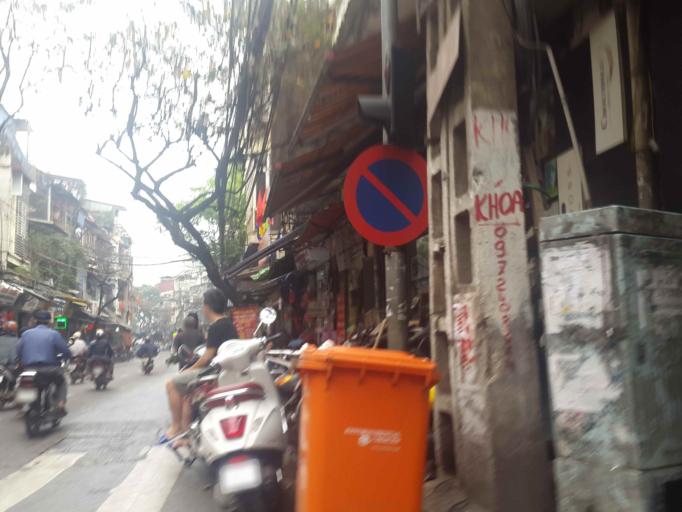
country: VN
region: Ha Noi
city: Hoan Kiem
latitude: 21.0340
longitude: 105.8499
